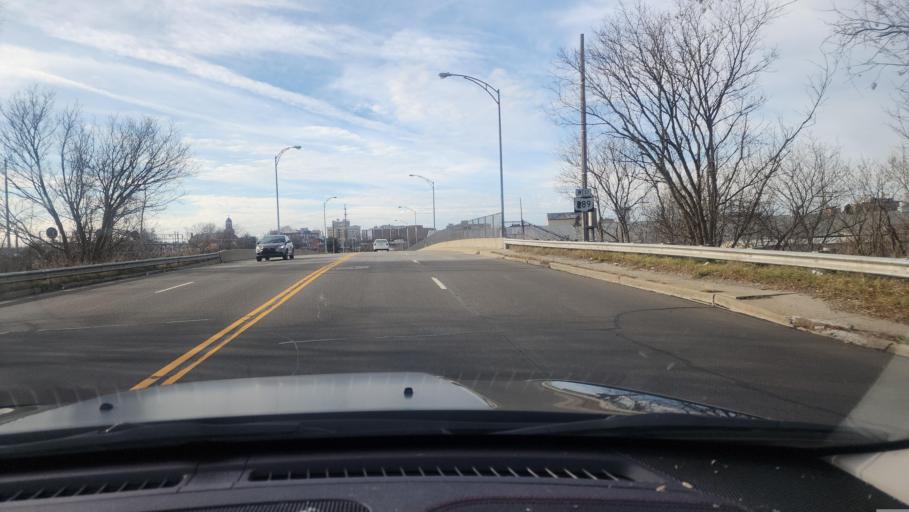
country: US
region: Ohio
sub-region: Mahoning County
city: Youngstown
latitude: 41.1007
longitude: -80.6371
